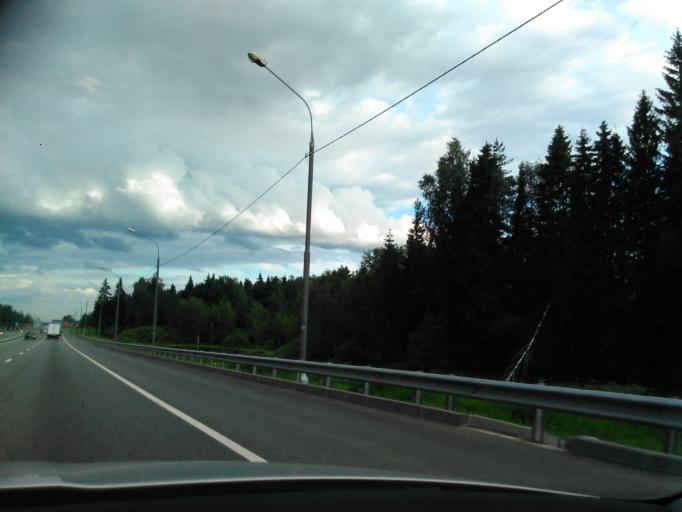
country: RU
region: Moskovskaya
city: Lozhki
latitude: 56.0844
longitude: 37.1185
